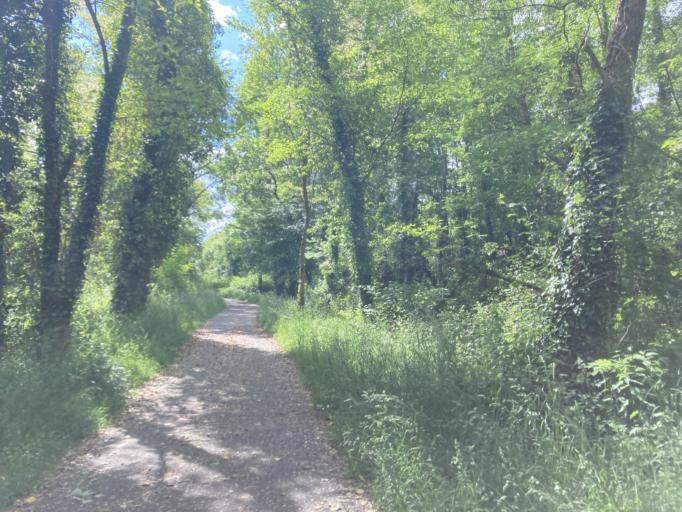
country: FR
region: Aquitaine
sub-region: Departement des Pyrenees-Atlantiques
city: Billere
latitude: 43.2991
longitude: -0.4198
